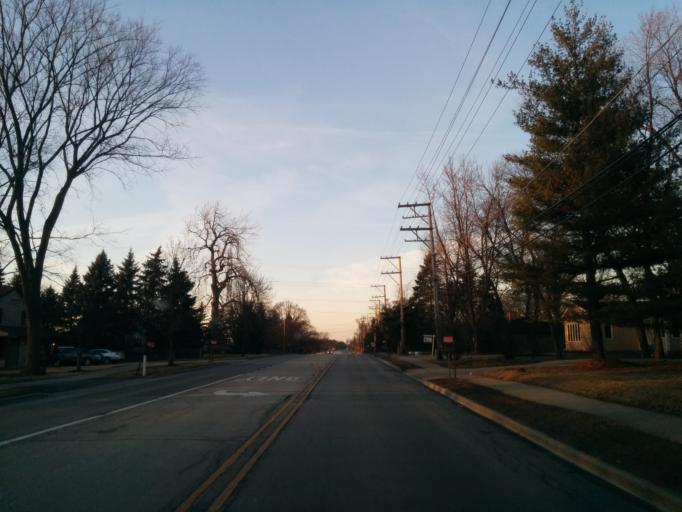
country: US
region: Illinois
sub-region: DuPage County
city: Glendale Heights
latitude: 41.9080
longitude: -88.0423
